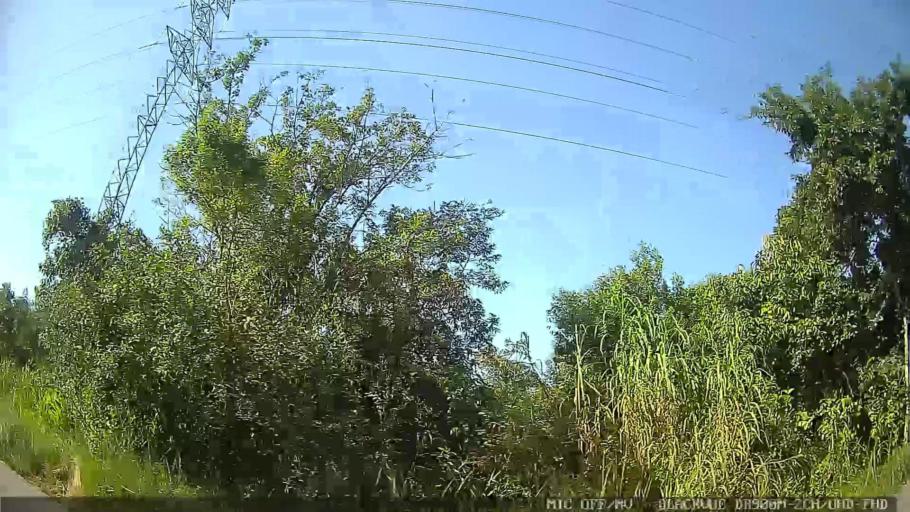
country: BR
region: Sao Paulo
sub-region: Santos
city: Santos
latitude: -23.9012
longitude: -46.3044
